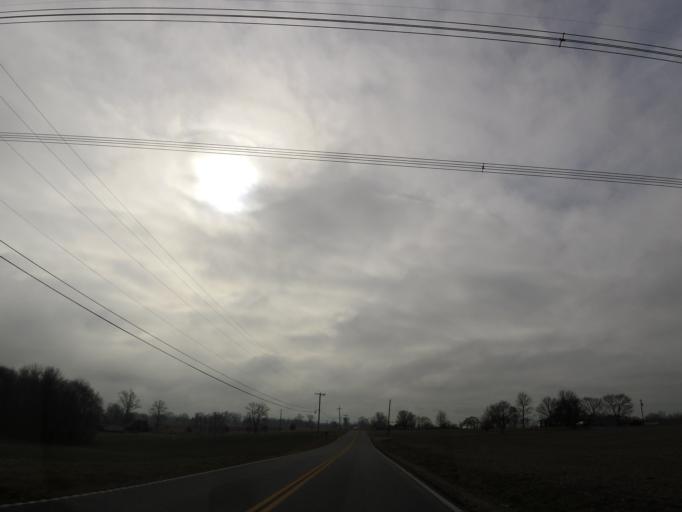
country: US
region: Kentucky
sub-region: Trimble County
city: Bedford
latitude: 38.6521
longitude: -85.3224
